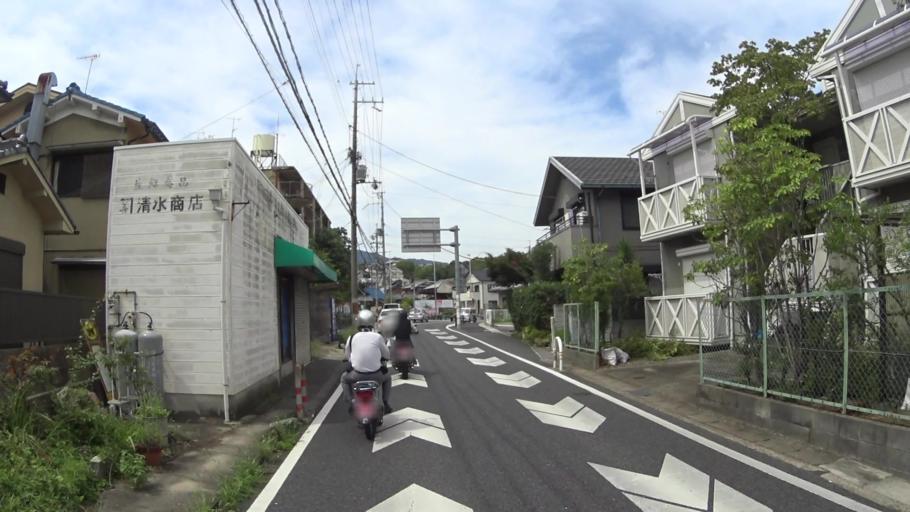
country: JP
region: Kyoto
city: Muko
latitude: 34.9649
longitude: 135.6950
